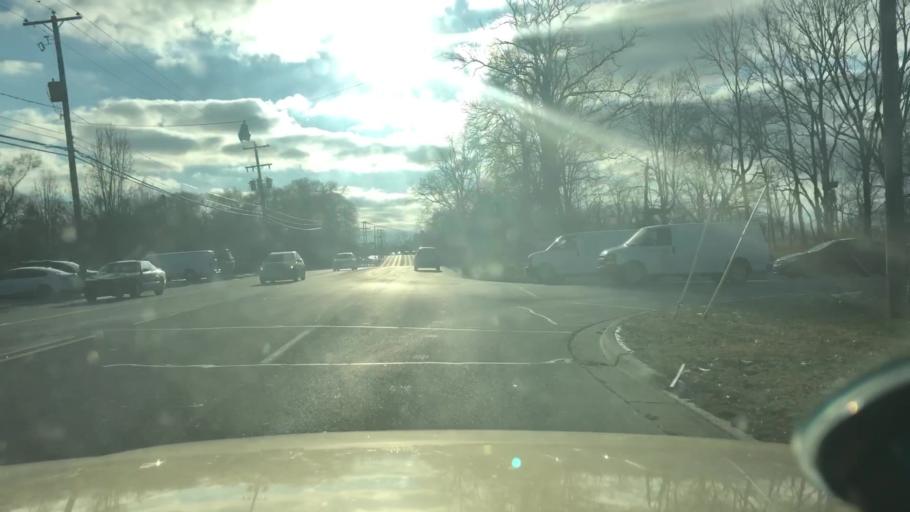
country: US
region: Michigan
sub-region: Jackson County
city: Vandercook Lake
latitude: 42.2045
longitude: -84.4335
